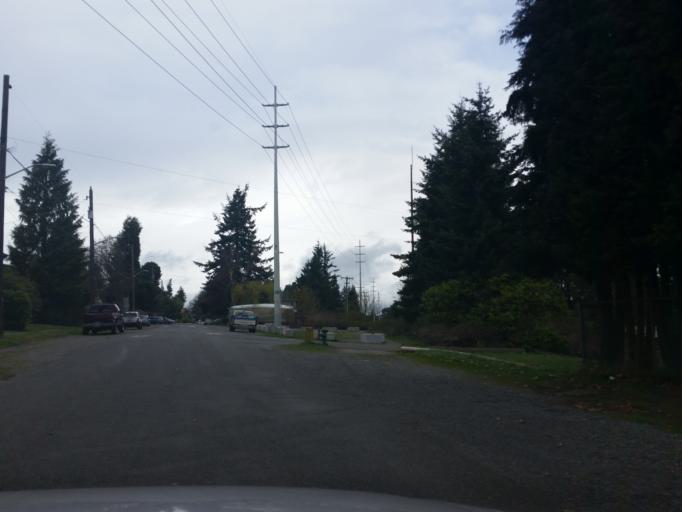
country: US
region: Washington
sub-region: King County
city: Shoreline
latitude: 47.7076
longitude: -122.3501
